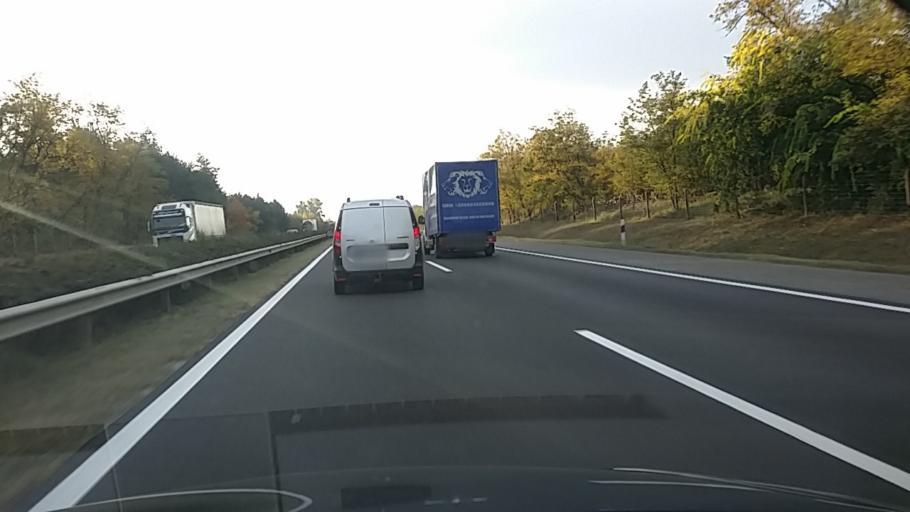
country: HU
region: Pest
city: Hernad
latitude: 47.1772
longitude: 19.4395
